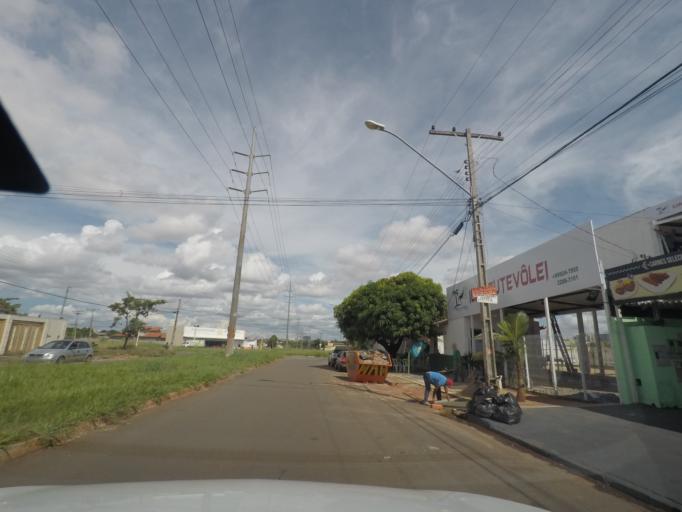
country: BR
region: Goias
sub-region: Goiania
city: Goiania
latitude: -16.7178
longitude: -49.3449
